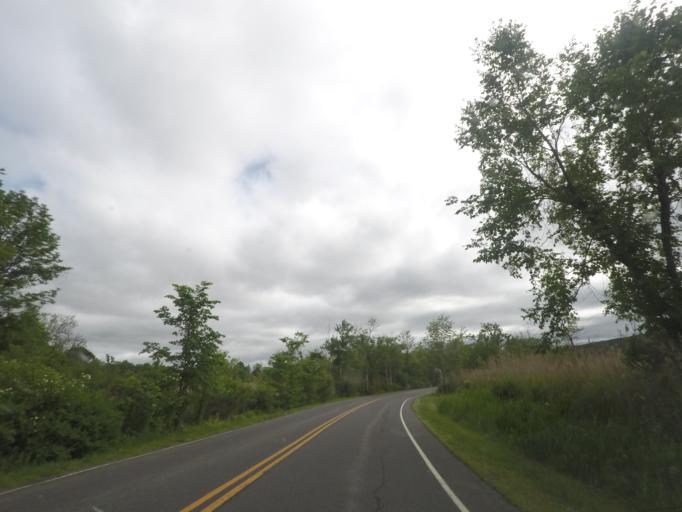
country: US
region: New York
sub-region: Dutchess County
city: Pine Plains
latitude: 41.9976
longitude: -73.5079
